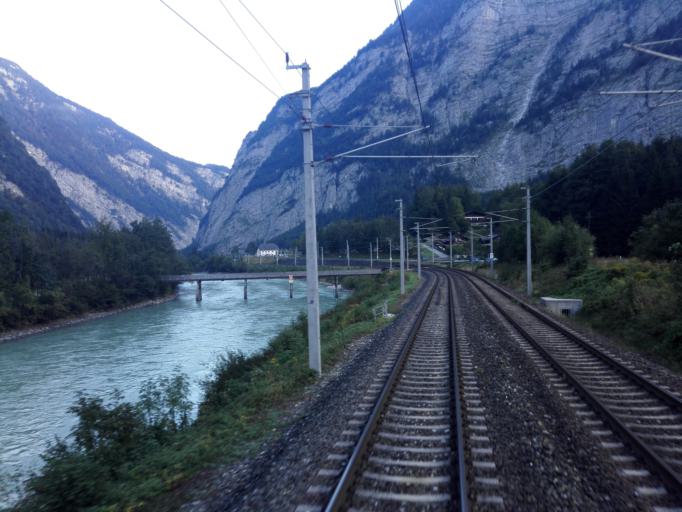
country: AT
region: Salzburg
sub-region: Politischer Bezirk Hallein
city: Golling an der Salzach
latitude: 47.5404
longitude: 13.1708
